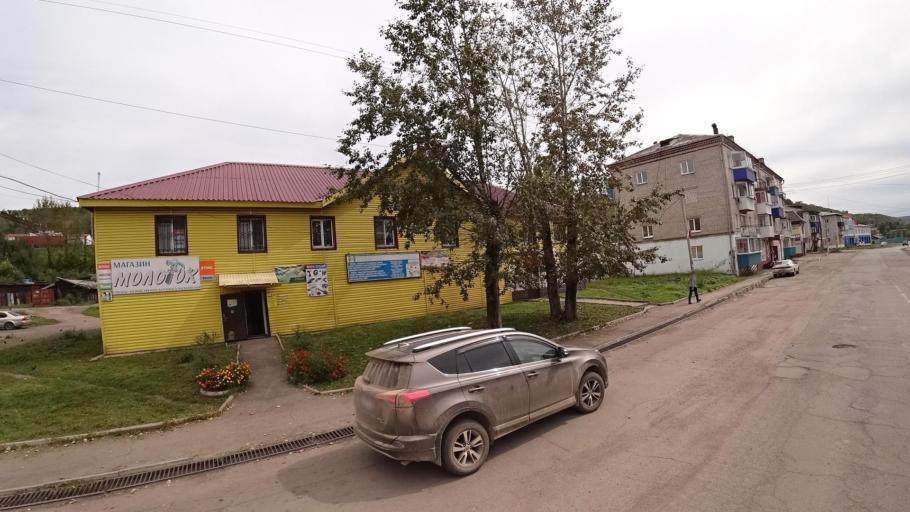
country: RU
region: Jewish Autonomous Oblast
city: Khingansk
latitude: 49.0101
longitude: 131.0573
